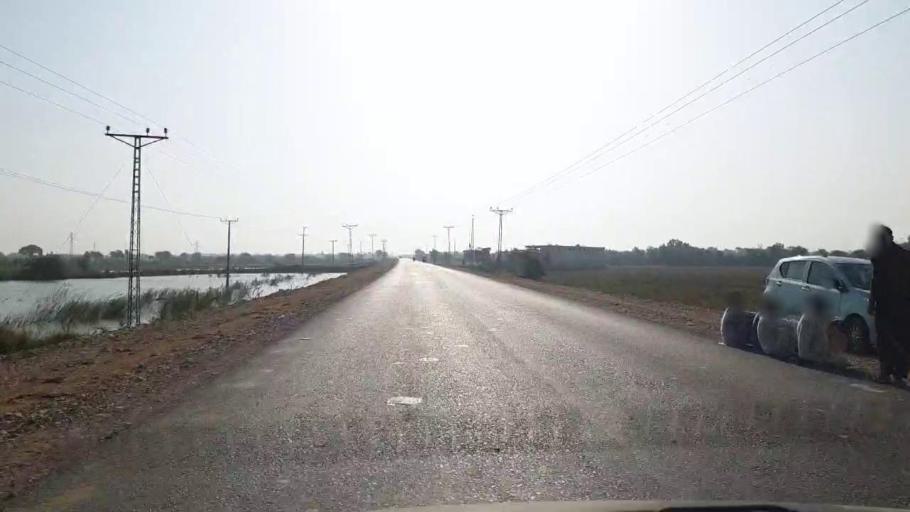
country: PK
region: Sindh
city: Badin
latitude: 24.6728
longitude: 68.8552
